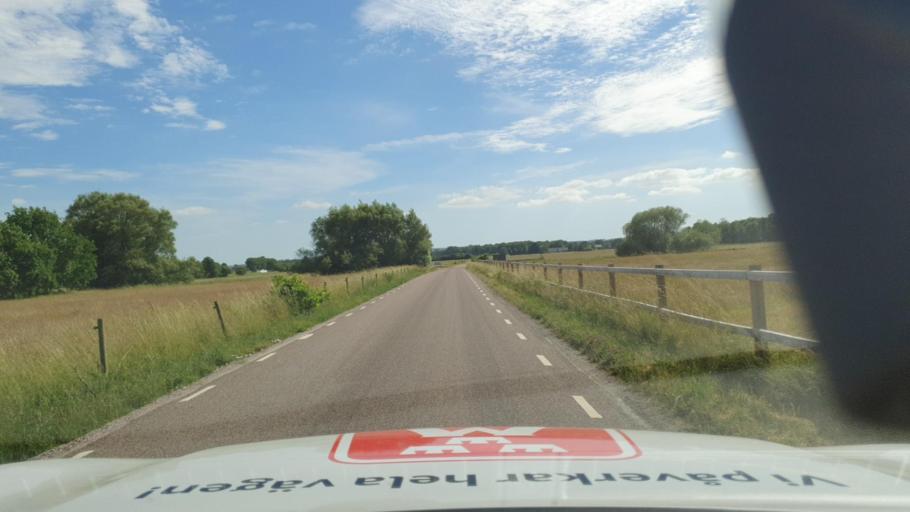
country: SE
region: Skane
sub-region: Sjobo Kommun
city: Blentarp
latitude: 55.6230
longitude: 13.6261
